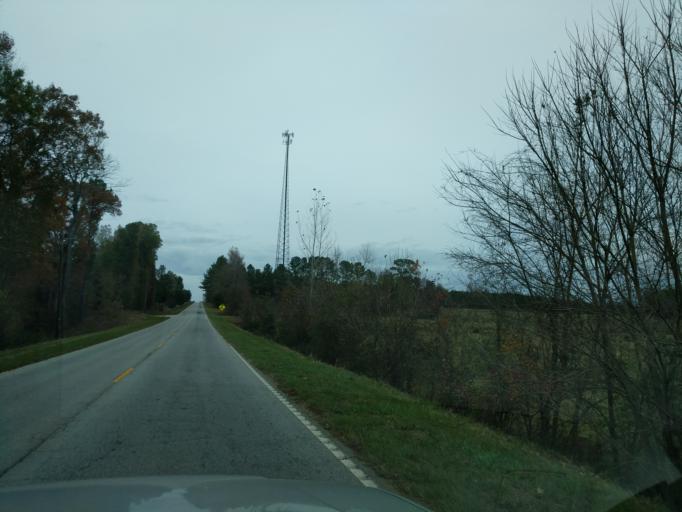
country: US
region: South Carolina
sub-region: Saluda County
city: Saluda
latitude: 34.0616
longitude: -81.7632
